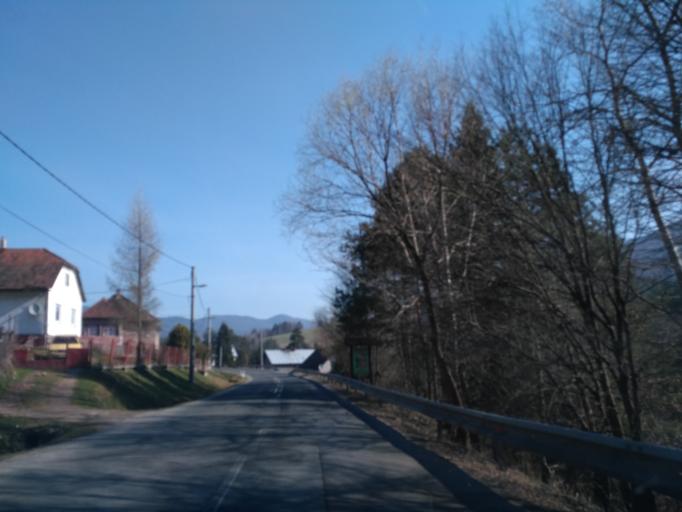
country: SK
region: Kosicky
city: Medzev
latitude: 48.7932
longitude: 20.8057
